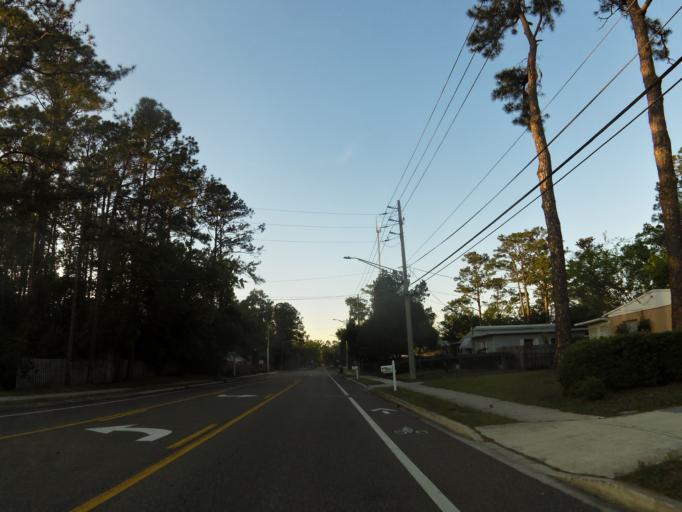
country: US
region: Florida
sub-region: Duval County
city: Jacksonville
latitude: 30.2722
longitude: -81.5711
